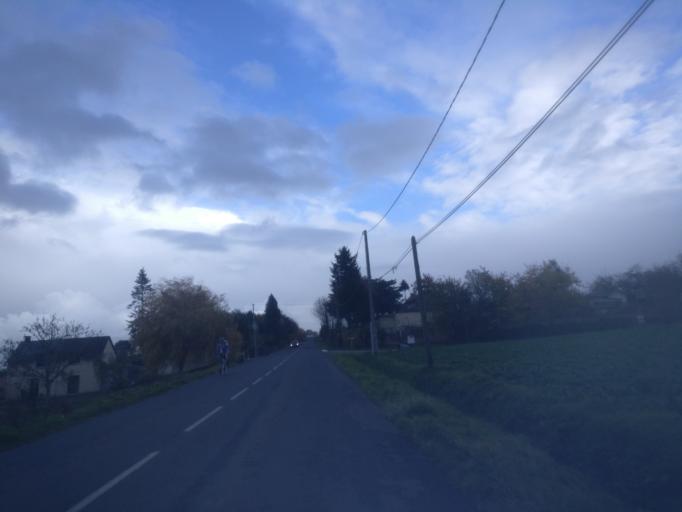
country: FR
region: Brittany
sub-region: Departement d'Ille-et-Vilaine
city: Breal-sous-Montfort
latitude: 48.0367
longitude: -1.8348
